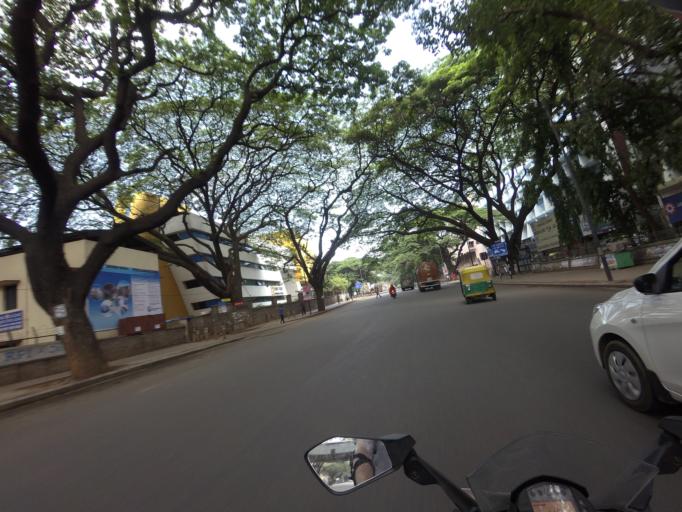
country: IN
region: Karnataka
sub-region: Bangalore Urban
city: Bangalore
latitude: 12.9716
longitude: 77.5832
